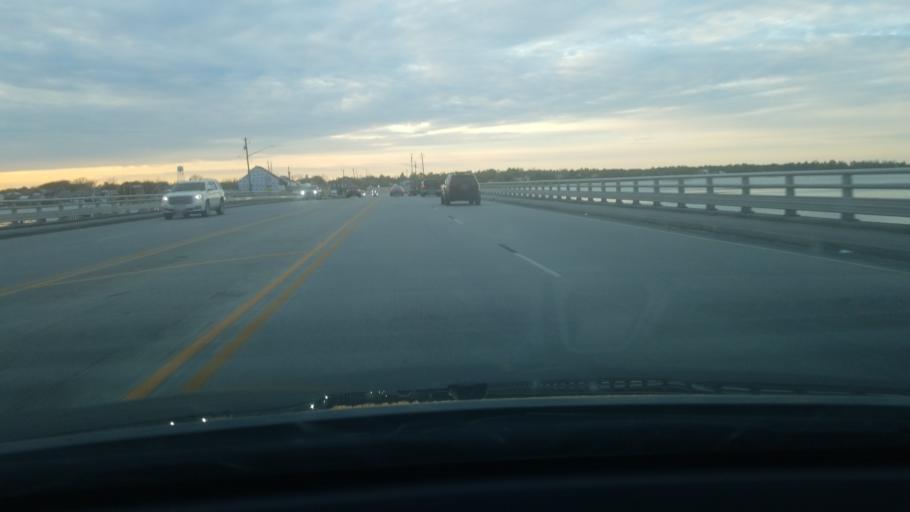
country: US
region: North Carolina
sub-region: Onslow County
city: Swansboro
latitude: 34.6829
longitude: -77.1128
